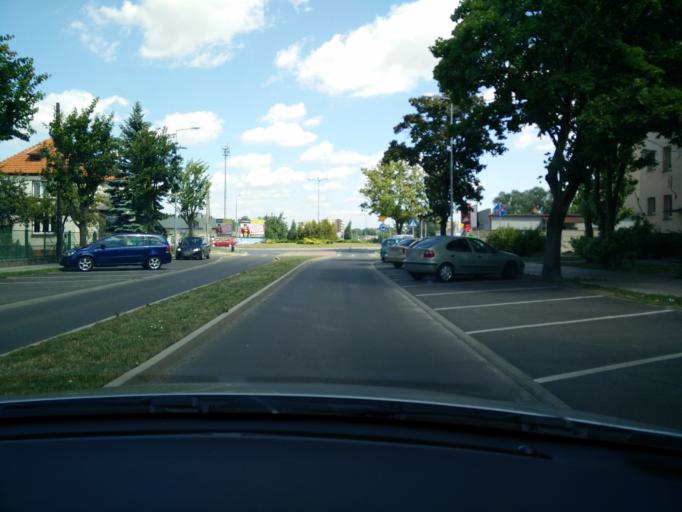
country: PL
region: Greater Poland Voivodeship
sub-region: Powiat sredzki
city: Sroda Wielkopolska
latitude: 52.2313
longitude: 17.2658
